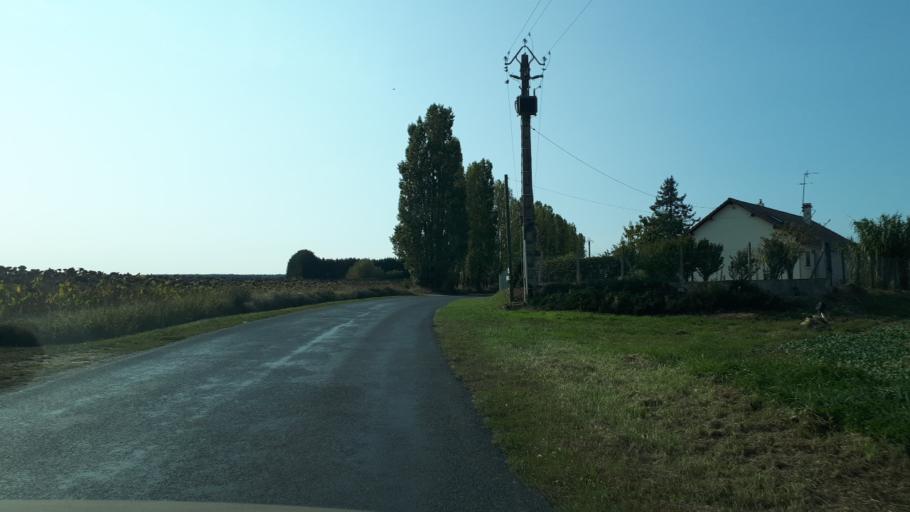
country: FR
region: Centre
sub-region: Departement du Cher
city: Vasselay
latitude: 47.2076
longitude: 2.4002
